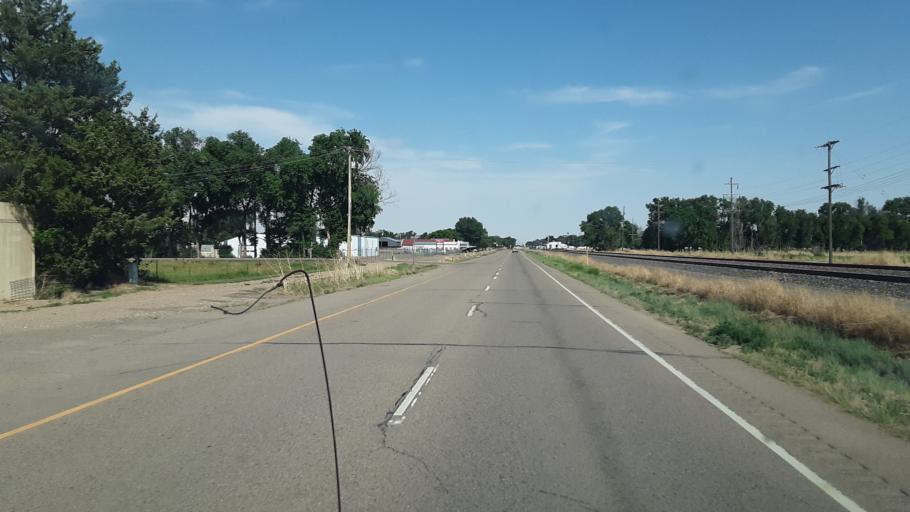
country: US
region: Colorado
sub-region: Otero County
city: Rocky Ford
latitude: 38.0601
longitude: -103.7376
